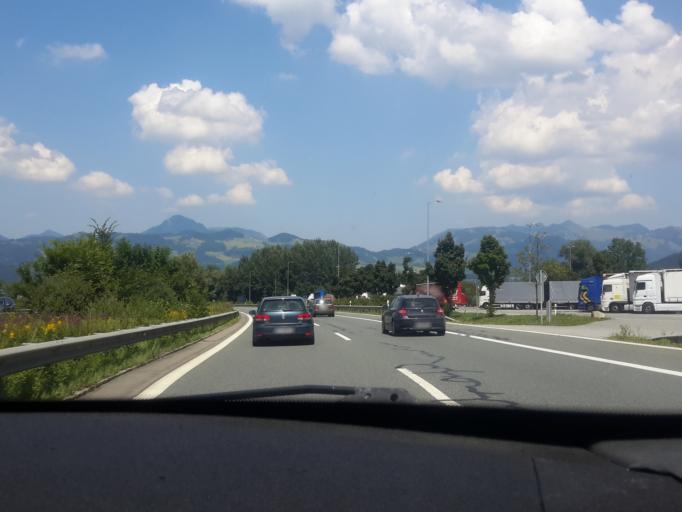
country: DE
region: Bavaria
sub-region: Upper Bavaria
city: Kiefersfelden
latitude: 47.6108
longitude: 12.2007
